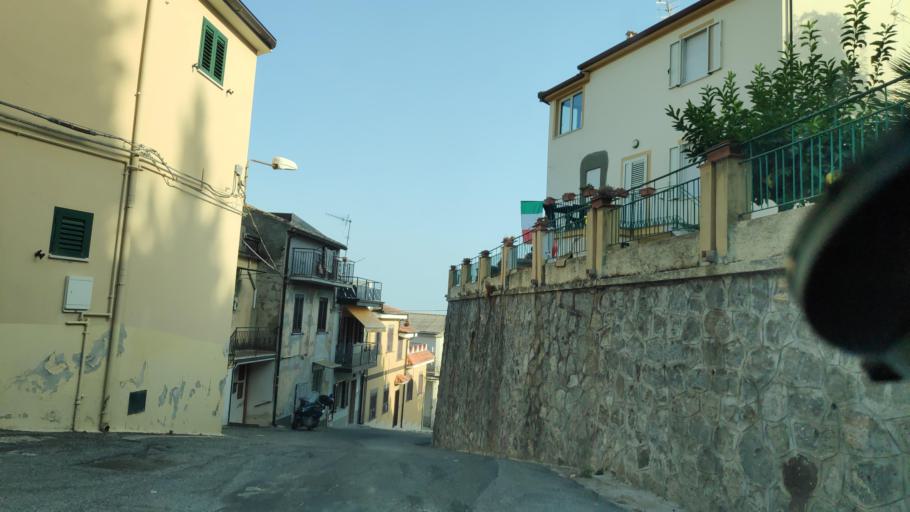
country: IT
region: Calabria
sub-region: Provincia di Catanzaro
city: Sant'Andrea Apostolo dello Ionio
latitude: 38.6196
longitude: 16.5318
